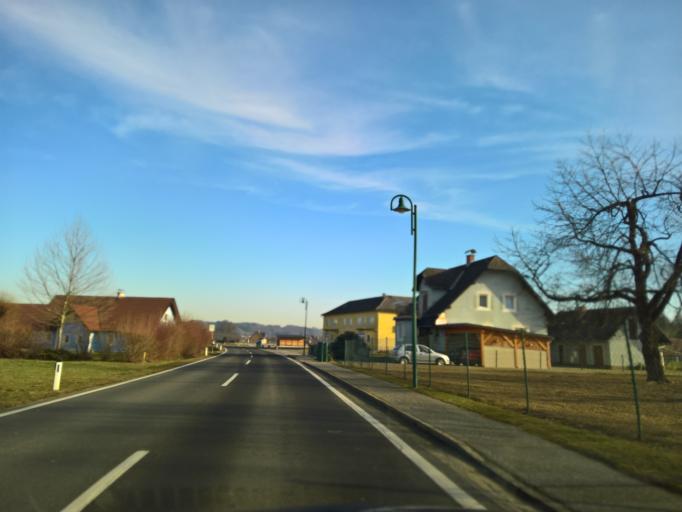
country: AT
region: Styria
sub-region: Politischer Bezirk Deutschlandsberg
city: Pitschgau
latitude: 46.6964
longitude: 15.2804
